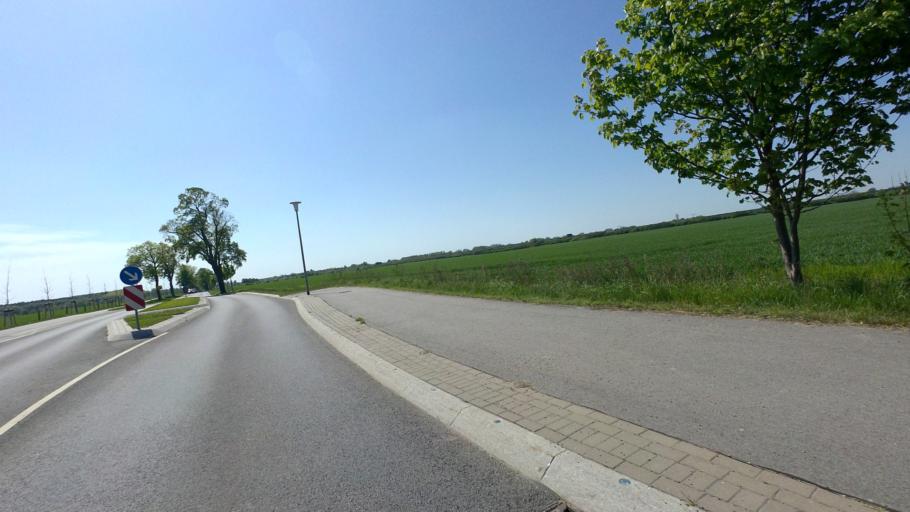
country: DE
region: Brandenburg
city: Schulzendorf
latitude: 52.3582
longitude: 13.5574
